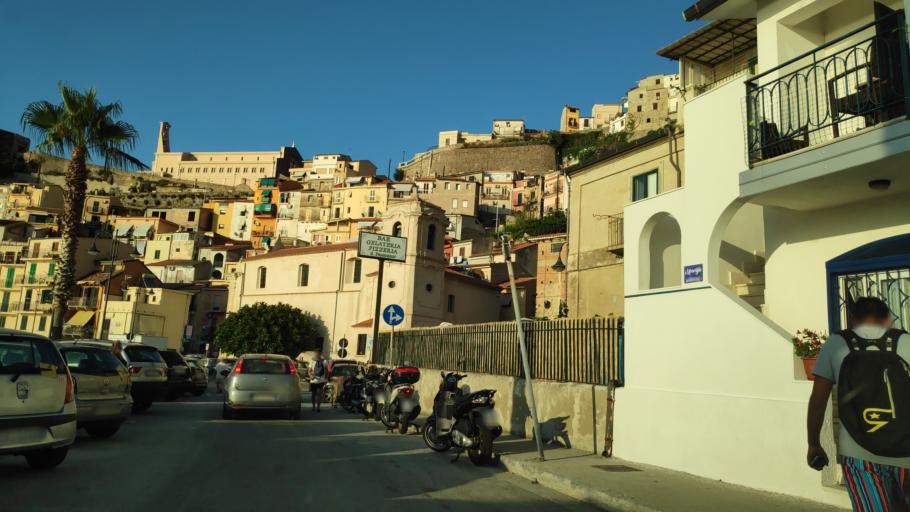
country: IT
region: Calabria
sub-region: Provincia di Reggio Calabria
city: Scilla
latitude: 38.2540
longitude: 15.7140
